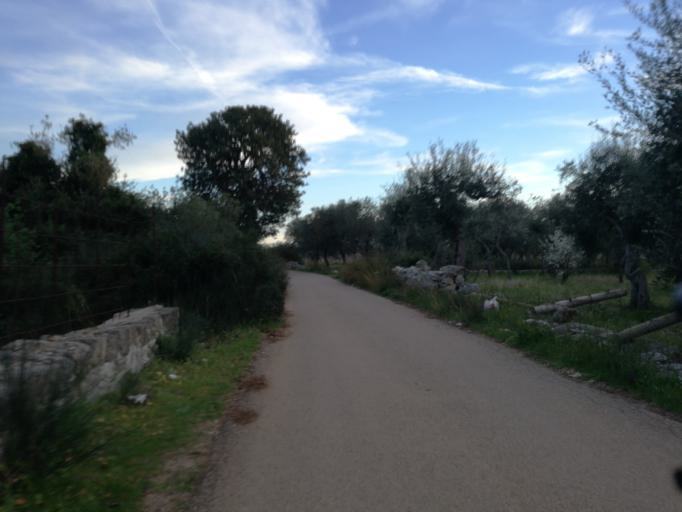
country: IT
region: Apulia
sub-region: Provincia di Bari
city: Lamie
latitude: 41.0229
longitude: 16.8718
